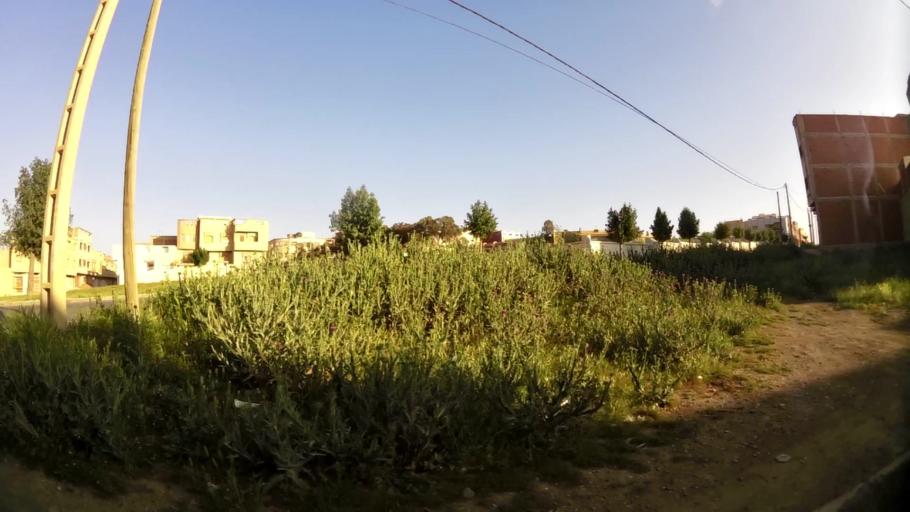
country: MA
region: Oriental
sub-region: Oujda-Angad
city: Oujda
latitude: 34.6745
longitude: -1.9410
